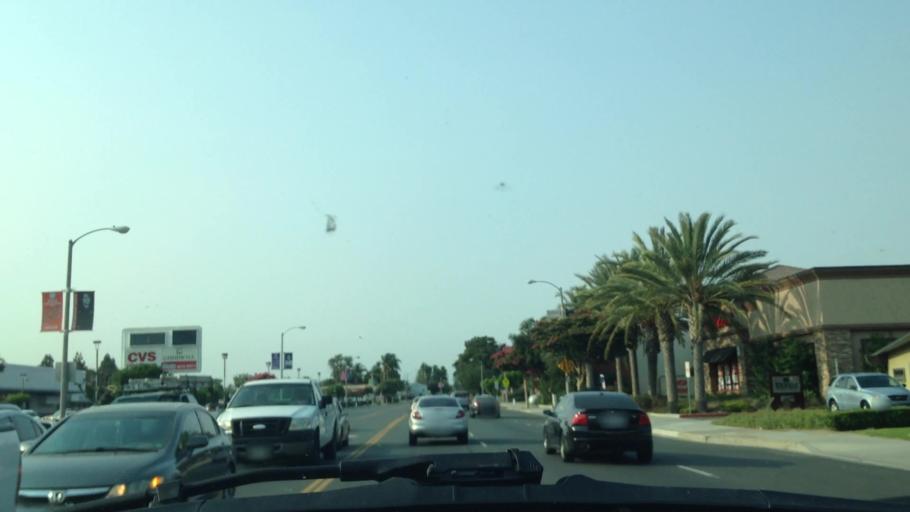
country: US
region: California
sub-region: Orange County
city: Santa Ana
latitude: 33.7604
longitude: -117.8519
